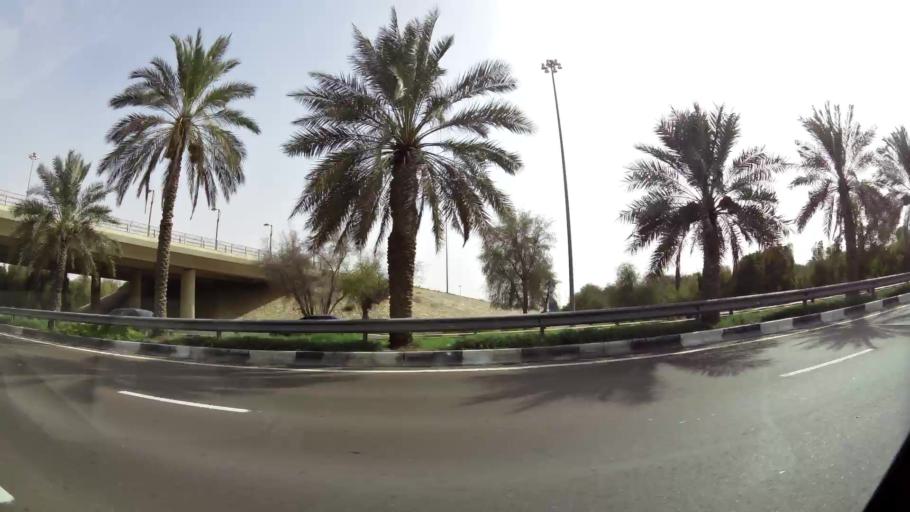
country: AE
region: Abu Dhabi
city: Al Ain
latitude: 24.1848
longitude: 55.5960
